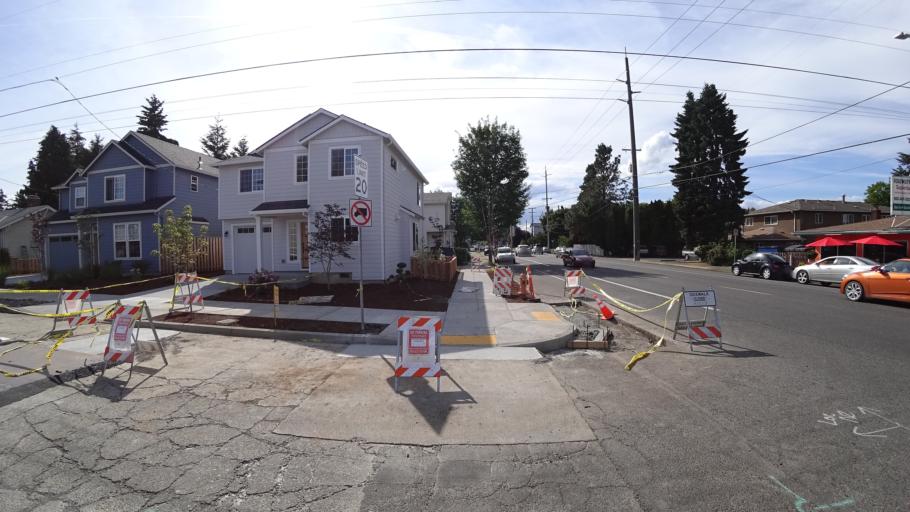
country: US
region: Oregon
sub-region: Washington County
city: West Haven
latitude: 45.5934
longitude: -122.7354
